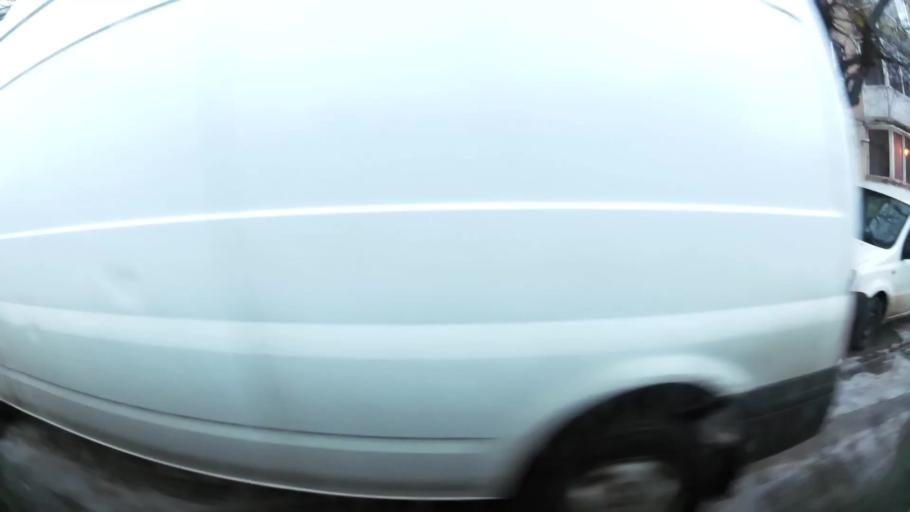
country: RO
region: Ilfov
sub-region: Comuna Chiajna
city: Rosu
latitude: 44.4311
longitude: 26.0230
